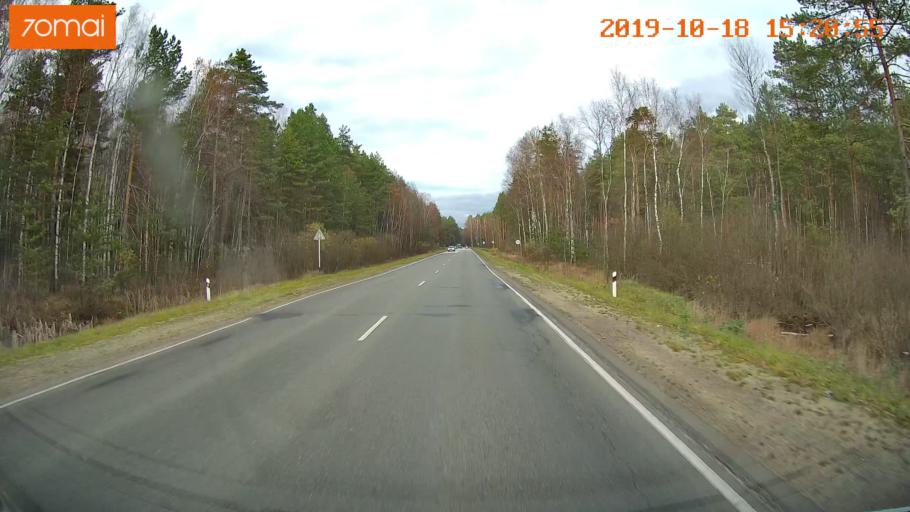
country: RU
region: Vladimir
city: Anopino
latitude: 55.6923
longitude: 40.7476
